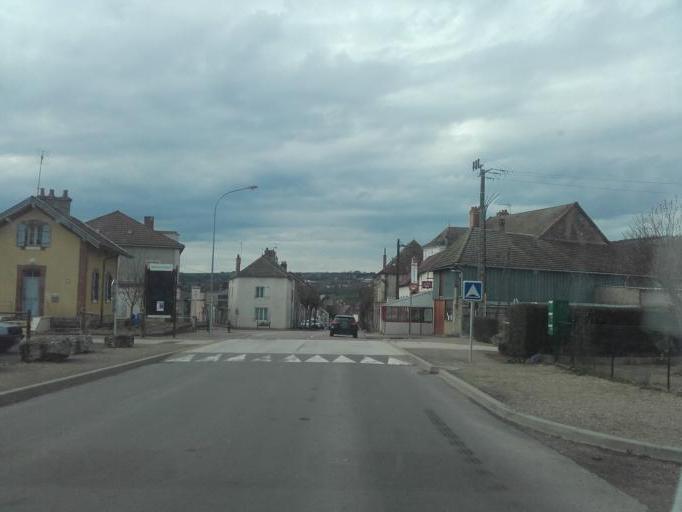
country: FR
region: Bourgogne
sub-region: Departement de la Cote-d'Or
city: Nolay
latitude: 46.9497
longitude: 4.6386
